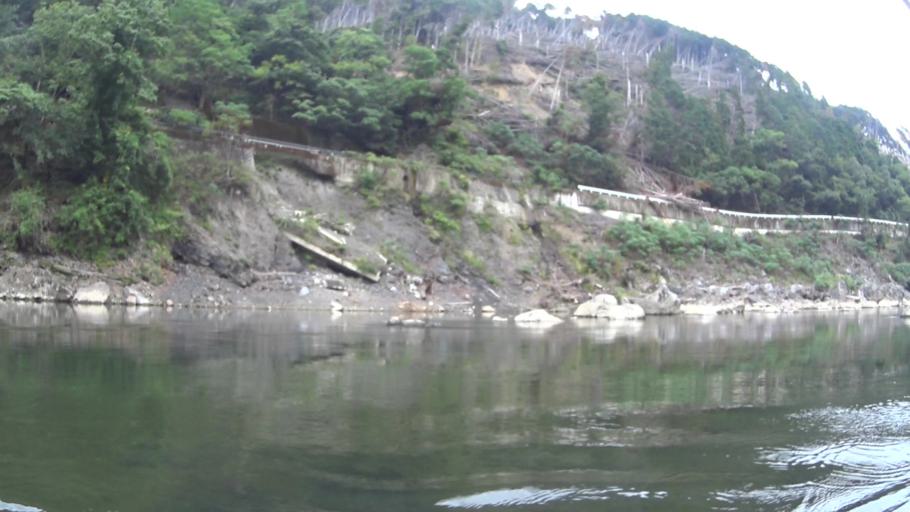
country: JP
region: Kyoto
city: Kameoka
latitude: 35.0227
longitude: 135.6151
